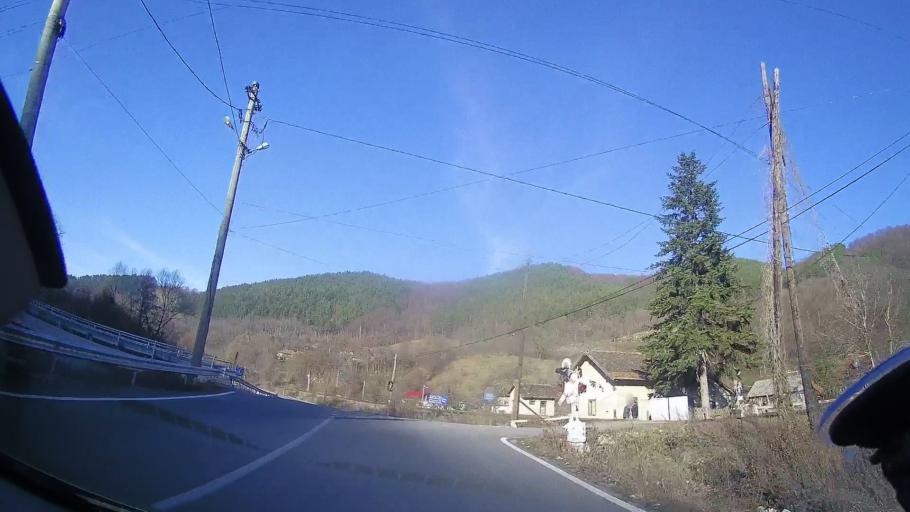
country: RO
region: Bihor
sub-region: Comuna Bratca
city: Bratca
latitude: 46.9272
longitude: 22.6474
